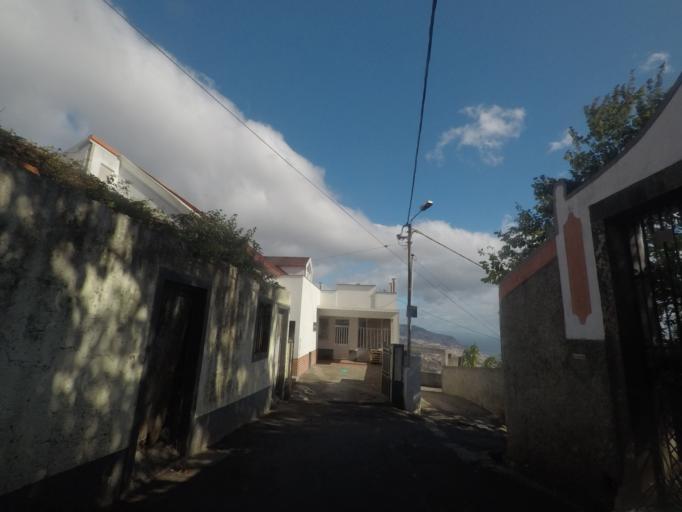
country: PT
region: Madeira
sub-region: Funchal
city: Nossa Senhora do Monte
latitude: 32.6719
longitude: -16.9435
